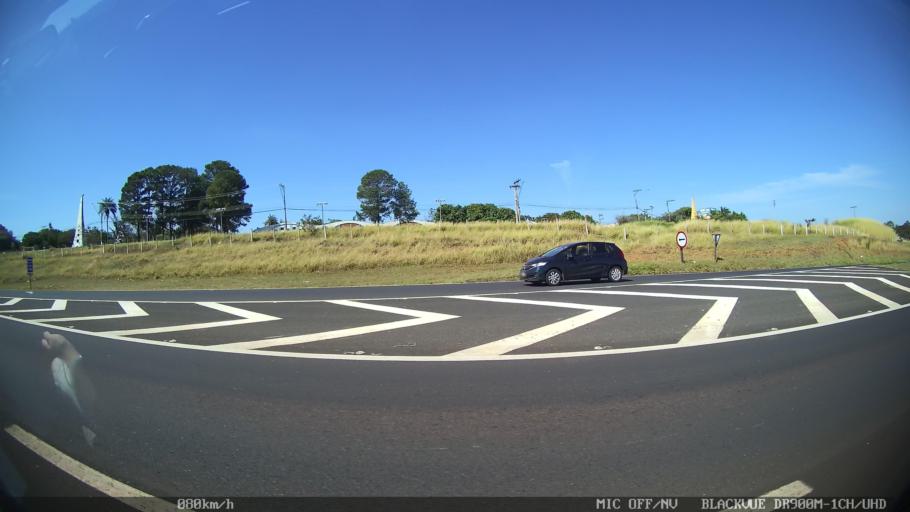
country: BR
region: Sao Paulo
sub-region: Franca
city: Franca
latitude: -20.5606
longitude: -47.4108
